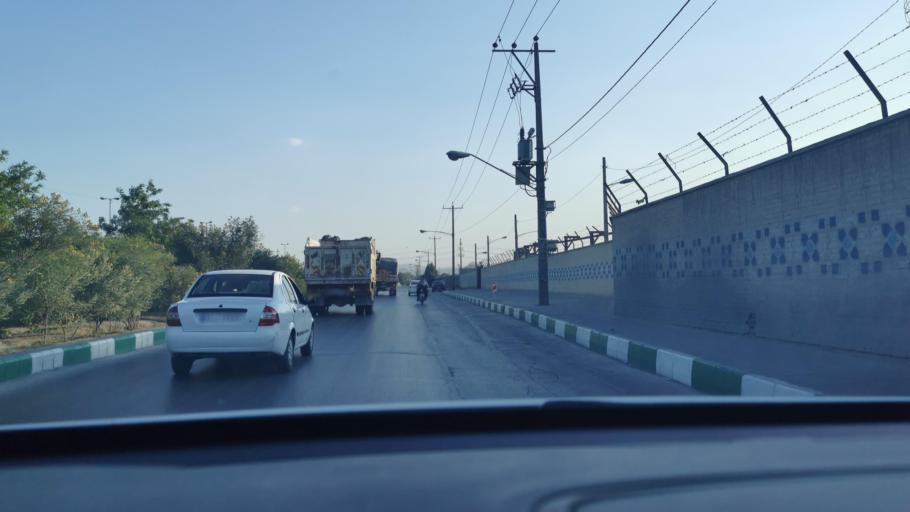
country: IR
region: Razavi Khorasan
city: Mashhad
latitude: 36.2672
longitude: 59.6542
